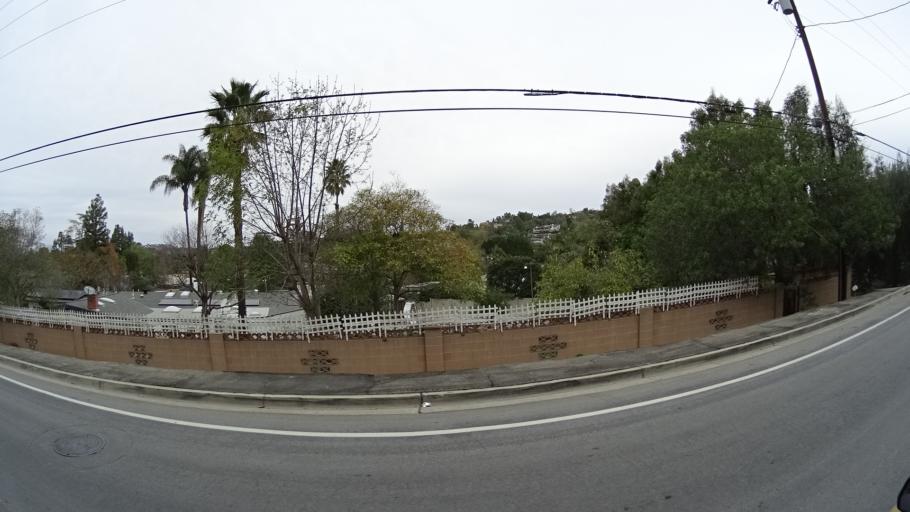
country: US
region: California
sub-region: Orange County
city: North Tustin
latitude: 33.7518
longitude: -117.7918
